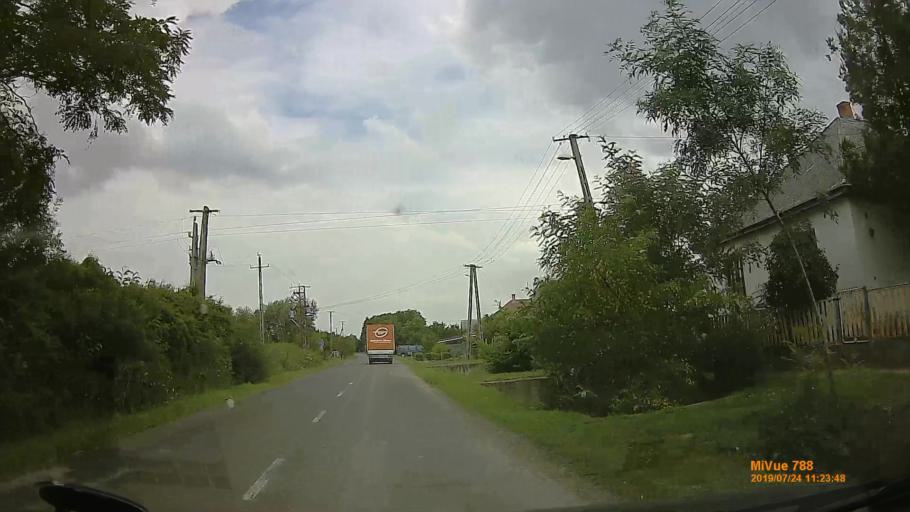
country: HU
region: Szabolcs-Szatmar-Bereg
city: Tarpa
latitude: 48.1943
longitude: 22.4537
